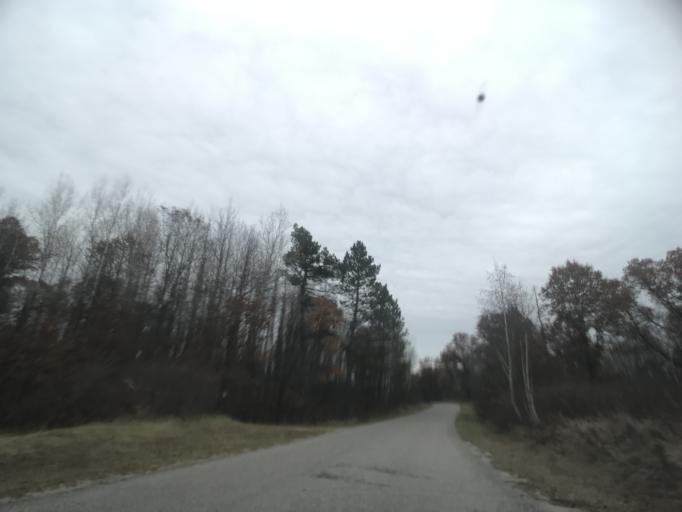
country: US
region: Wisconsin
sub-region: Oconto County
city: Gillett
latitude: 45.3489
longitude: -88.2860
